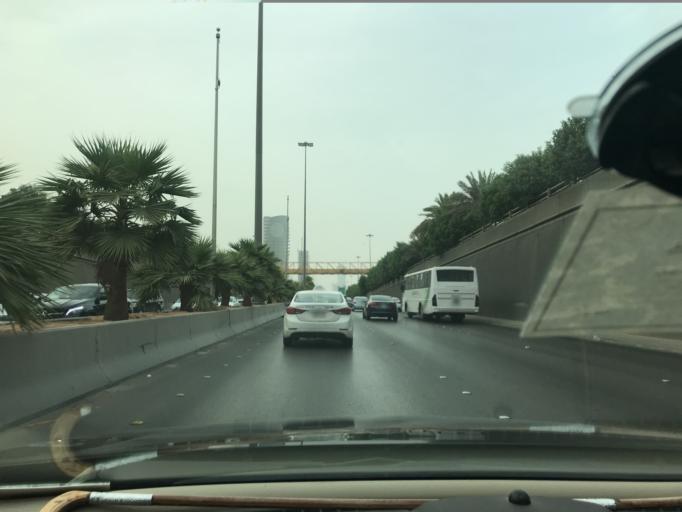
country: SA
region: Ar Riyad
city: Riyadh
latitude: 24.7131
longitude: 46.6713
